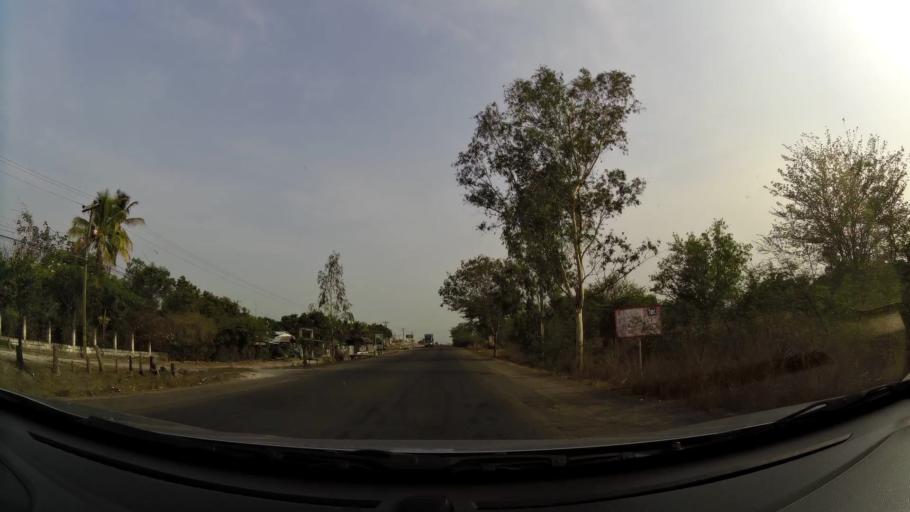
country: HN
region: Comayagua
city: Flores
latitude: 14.3056
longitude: -87.5775
